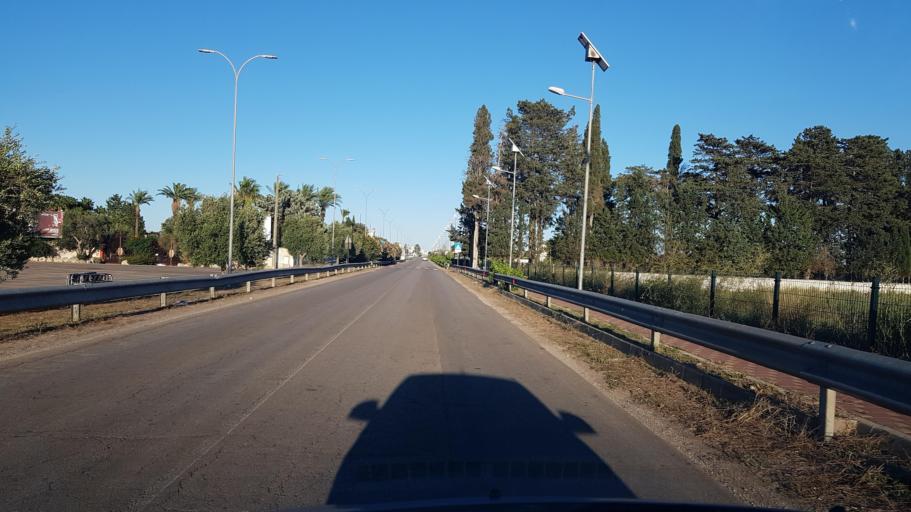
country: IT
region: Apulia
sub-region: Provincia di Brindisi
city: San Pancrazio Salentino
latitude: 40.4169
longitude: 17.8205
